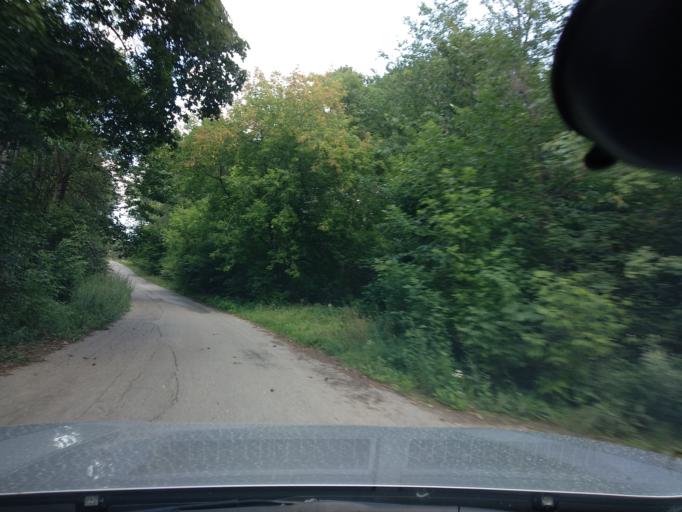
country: LT
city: Grigiskes
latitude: 54.6807
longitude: 25.0787
